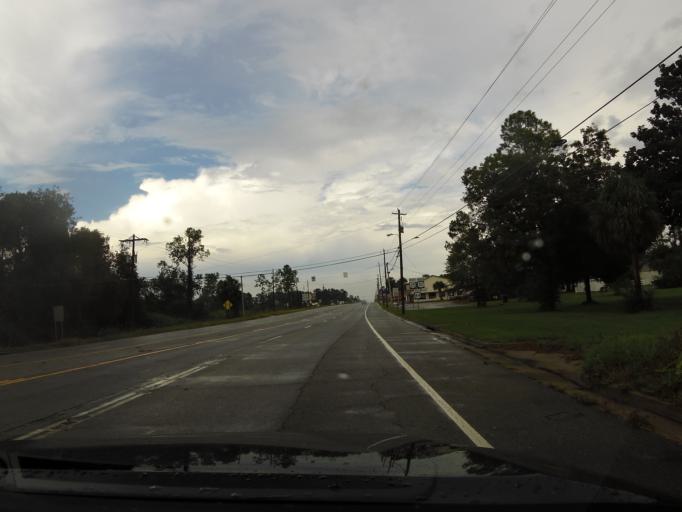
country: US
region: Georgia
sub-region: Wayne County
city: Jesup
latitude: 31.6262
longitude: -81.8668
